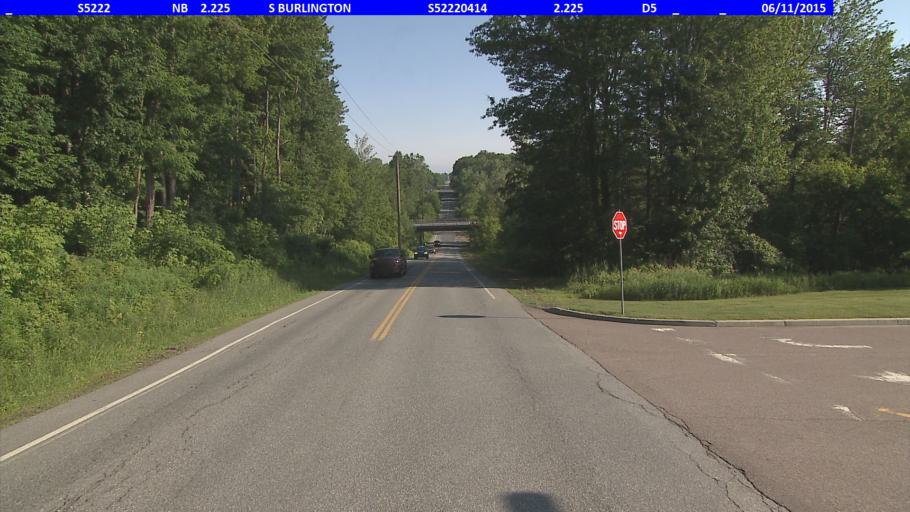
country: US
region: Vermont
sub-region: Chittenden County
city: South Burlington
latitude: 44.4486
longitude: -73.1881
